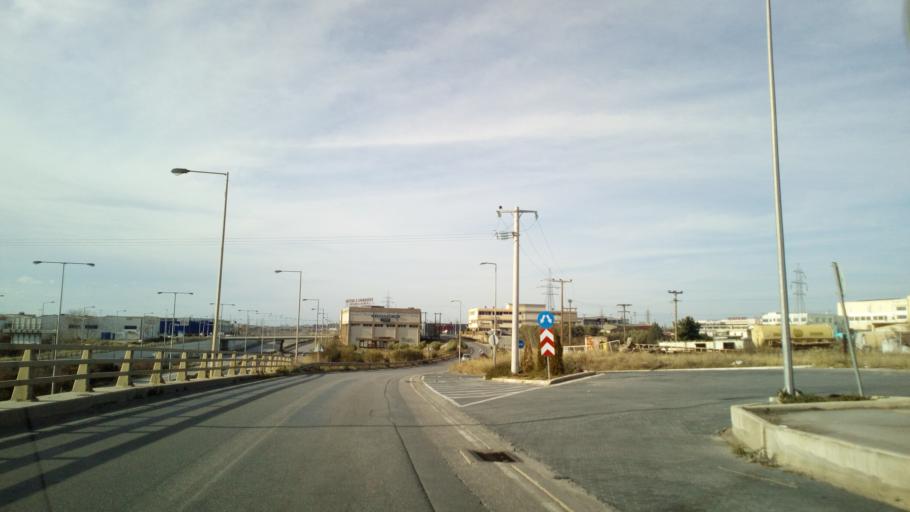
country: GR
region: Central Macedonia
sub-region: Nomos Thessalonikis
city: Efkarpia
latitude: 40.6961
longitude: 22.9446
